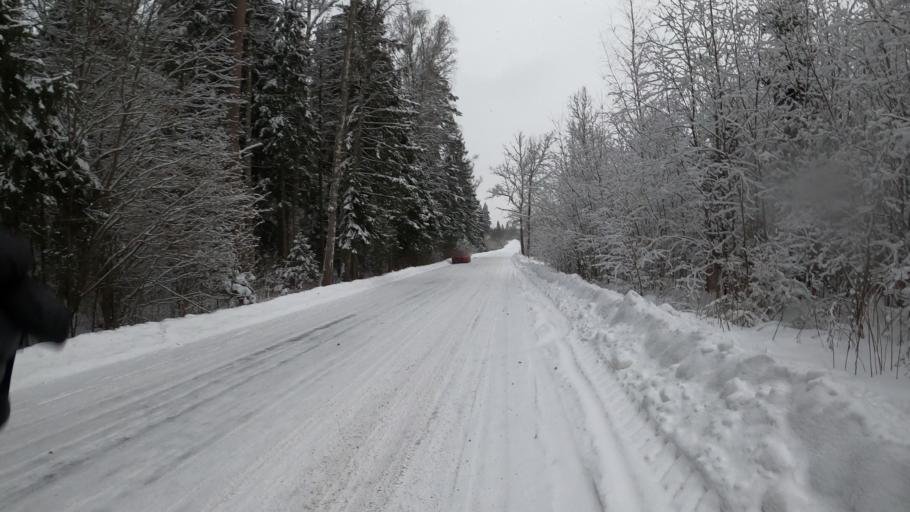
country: RU
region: Moskovskaya
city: Firsanovka
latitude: 55.9213
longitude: 37.2119
